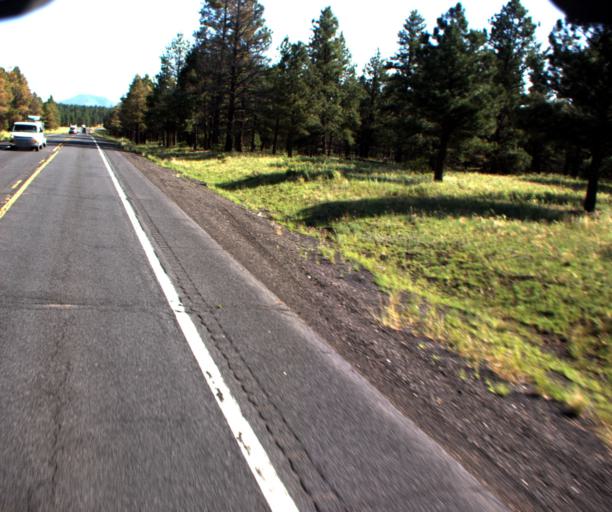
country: US
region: Arizona
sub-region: Coconino County
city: Williams
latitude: 35.2782
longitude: -112.1470
